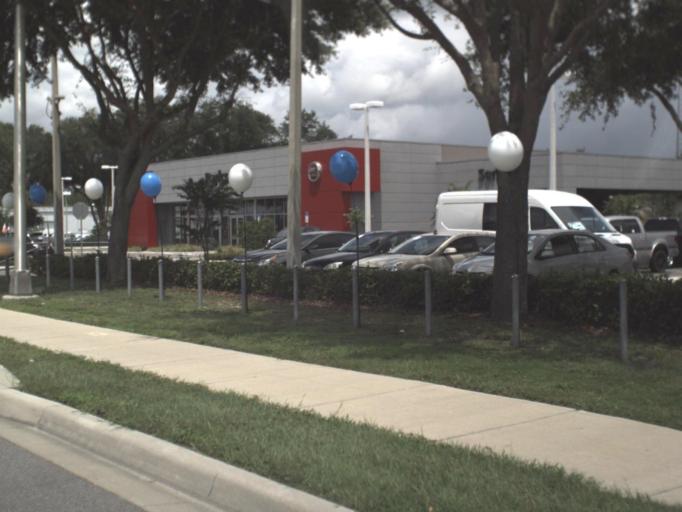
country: US
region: Florida
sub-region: Pasco County
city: Wesley Chapel
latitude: 28.2387
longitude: -82.3417
